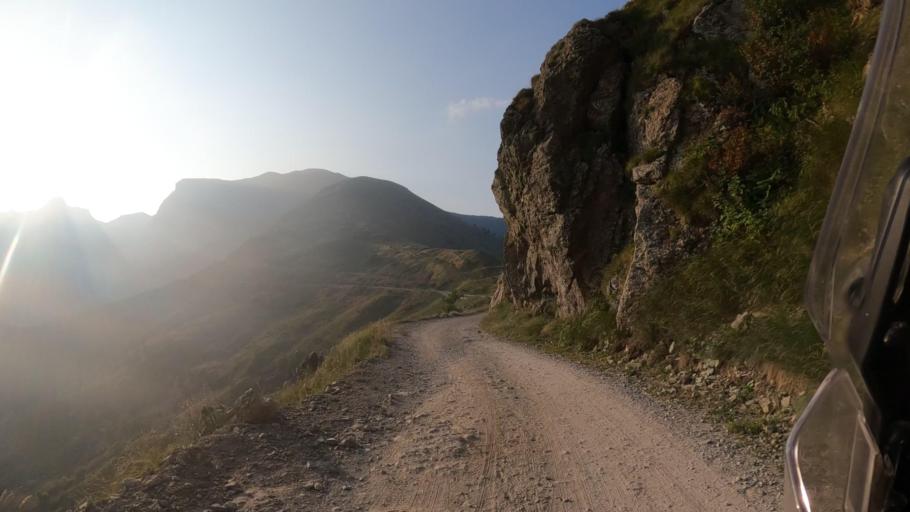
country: IT
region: Piedmont
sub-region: Provincia di Cuneo
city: Limone Piemonte
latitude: 44.1536
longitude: 7.5765
